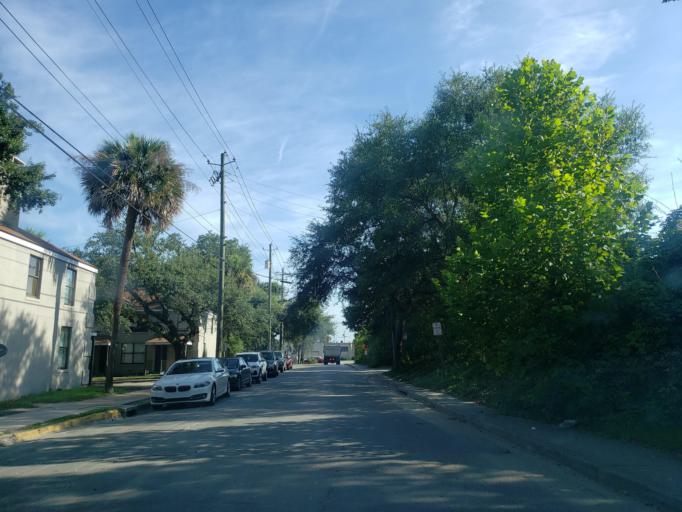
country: US
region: Georgia
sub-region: Chatham County
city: Savannah
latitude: 32.0811
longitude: -81.0983
